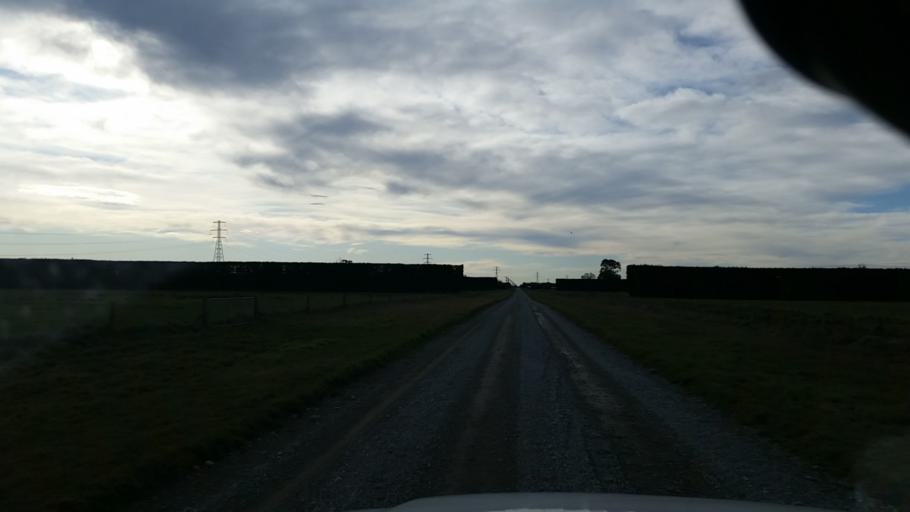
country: NZ
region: Canterbury
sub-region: Ashburton District
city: Tinwald
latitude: -44.0408
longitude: 171.4866
